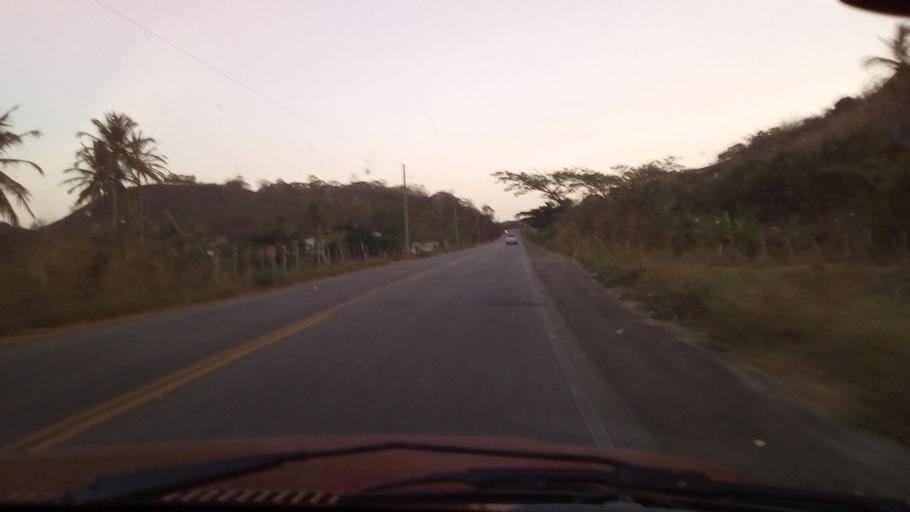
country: BR
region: Paraiba
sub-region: Bananeiras
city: Solanea
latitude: -6.7403
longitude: -35.5338
